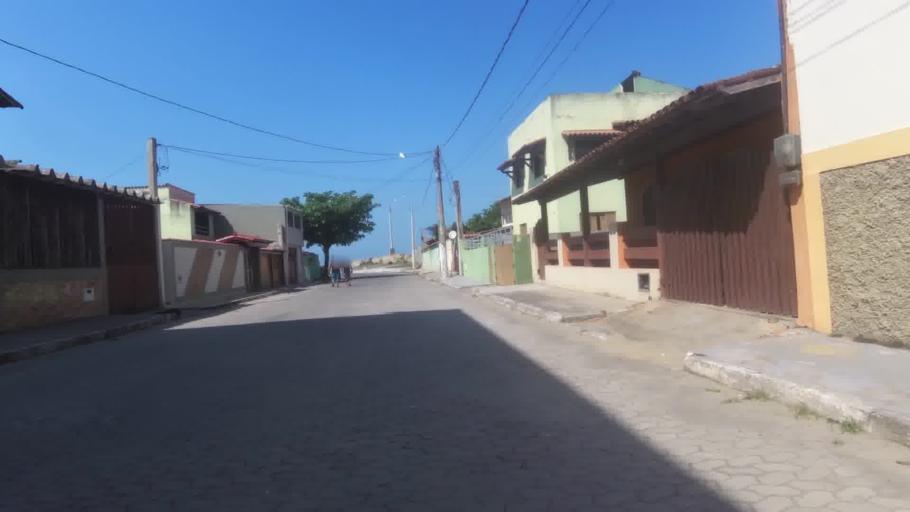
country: BR
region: Espirito Santo
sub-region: Marataizes
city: Marataizes
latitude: -21.0328
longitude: -40.8135
